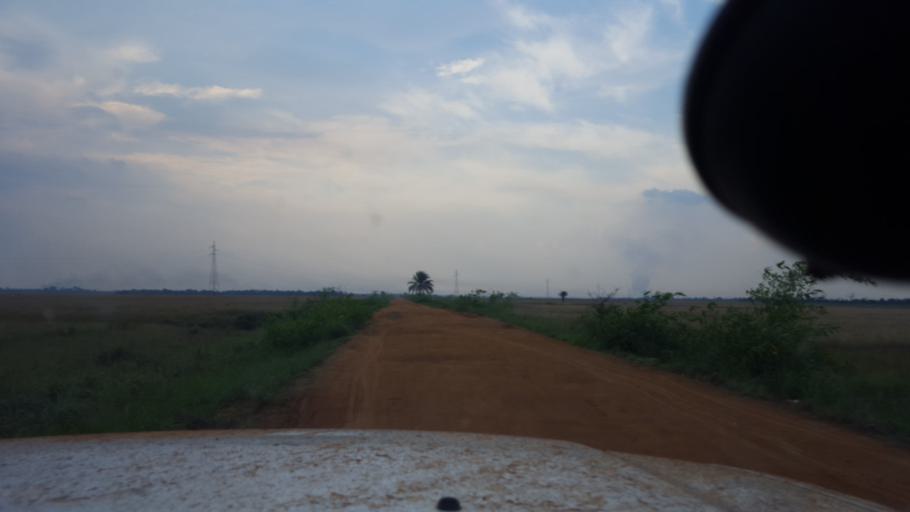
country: CD
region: Bandundu
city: Bandundu
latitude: -3.4033
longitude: 17.2571
